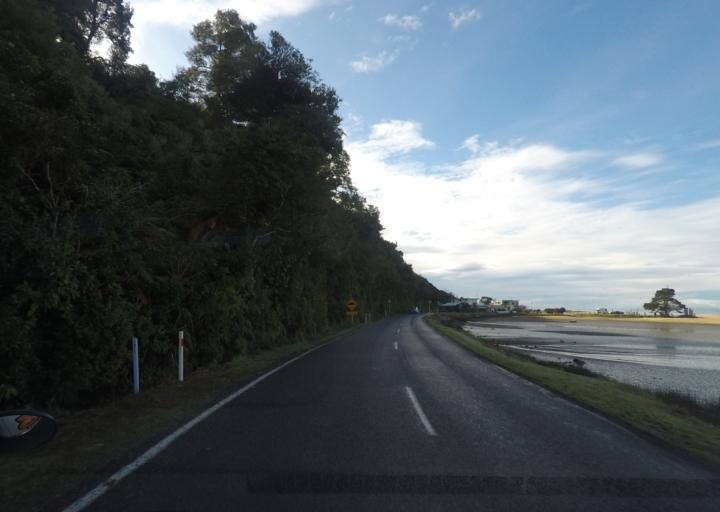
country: NZ
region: Tasman
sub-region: Tasman District
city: Motueka
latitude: -41.0094
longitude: 173.0054
